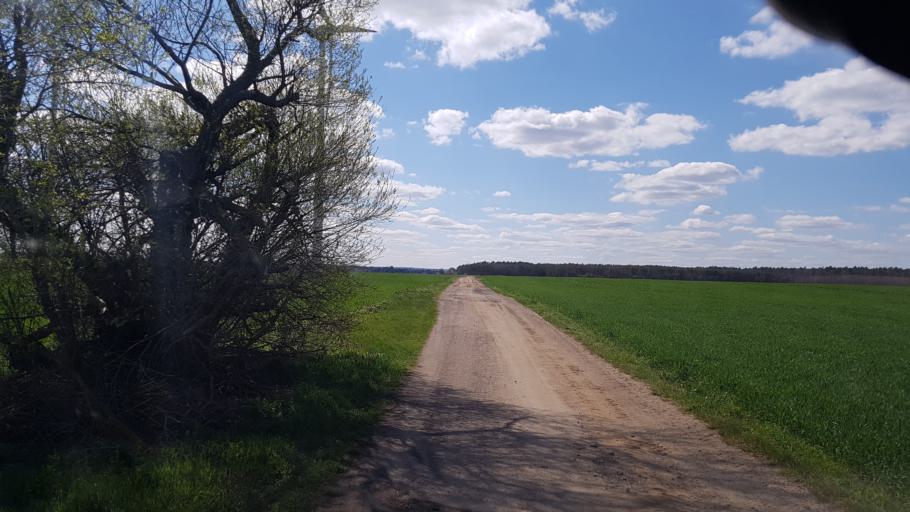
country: DE
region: Brandenburg
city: Muhlberg
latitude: 51.4700
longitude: 13.2503
